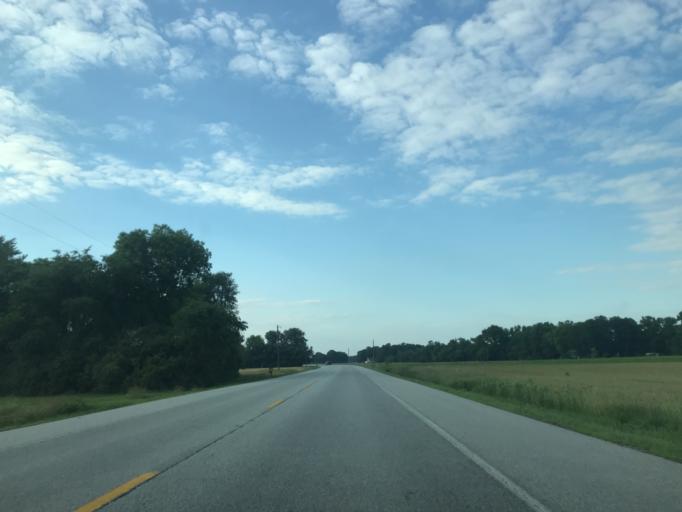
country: US
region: Maryland
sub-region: Caroline County
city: Federalsburg
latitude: 38.7693
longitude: -75.7875
